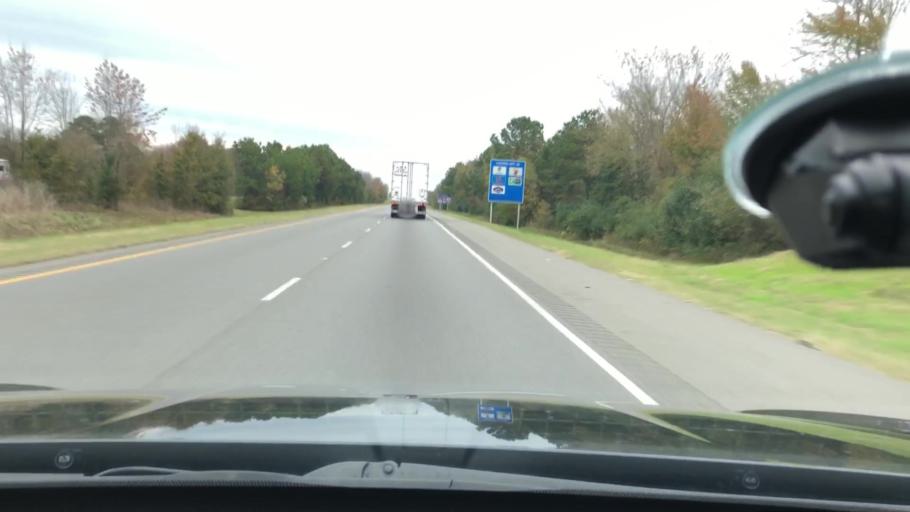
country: US
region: Arkansas
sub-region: Hempstead County
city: Hope
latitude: 33.6694
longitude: -93.6275
